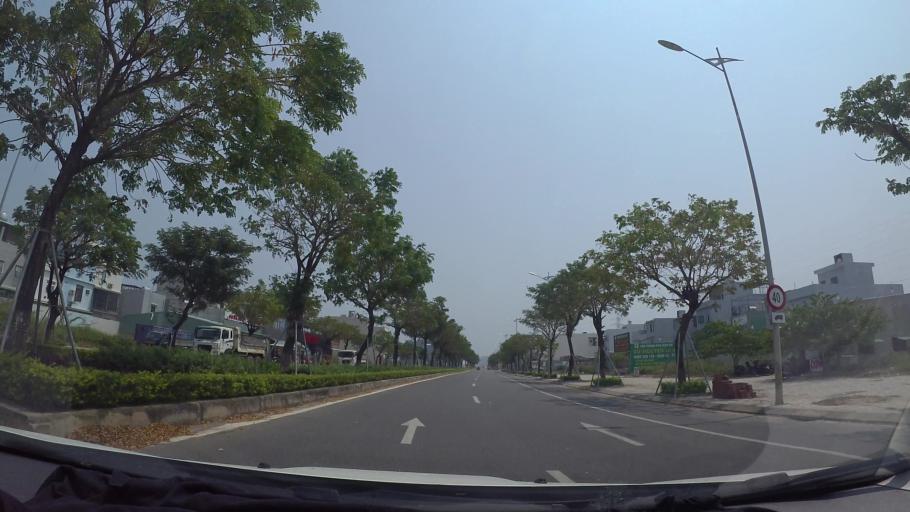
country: VN
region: Da Nang
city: Ngu Hanh Son
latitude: 16.0182
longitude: 108.2307
